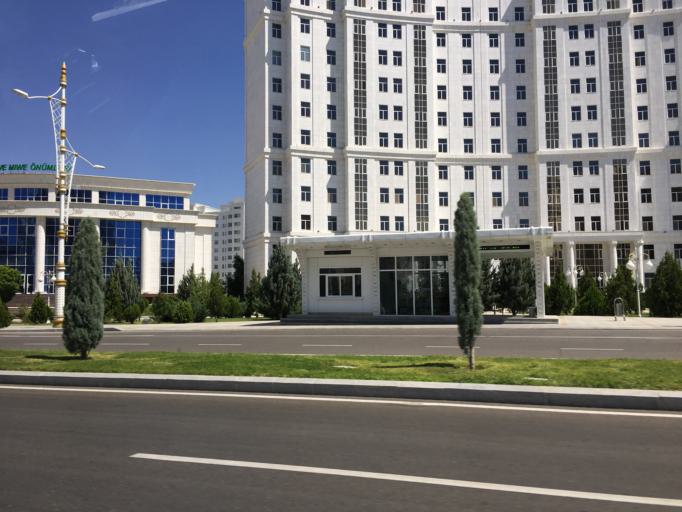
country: TM
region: Ahal
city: Ashgabat
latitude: 37.9223
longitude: 58.3624
